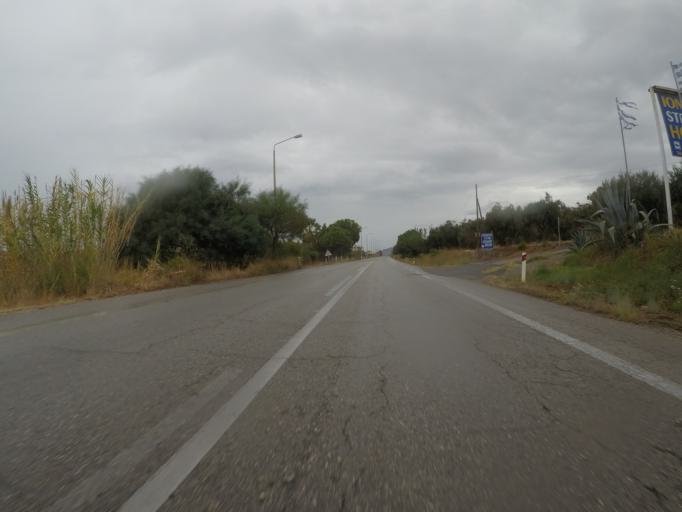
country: GR
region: West Greece
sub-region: Nomos Ileias
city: Zacharo
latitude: 37.4197
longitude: 21.6699
